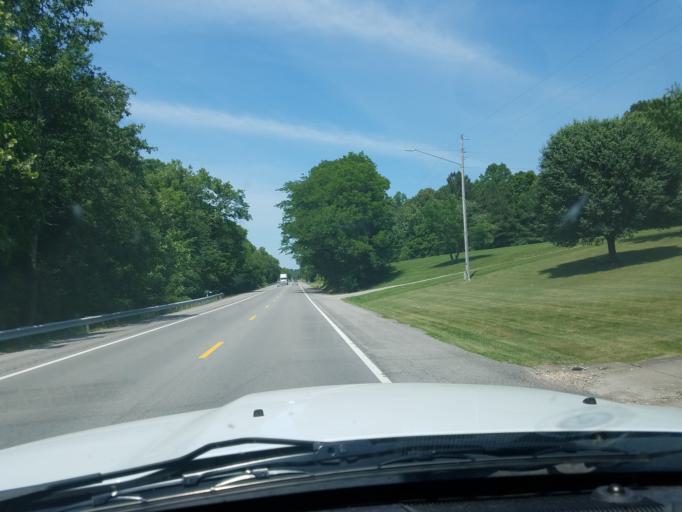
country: US
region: Tennessee
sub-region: Sumner County
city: Westmoreland
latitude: 36.5918
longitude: -86.2364
